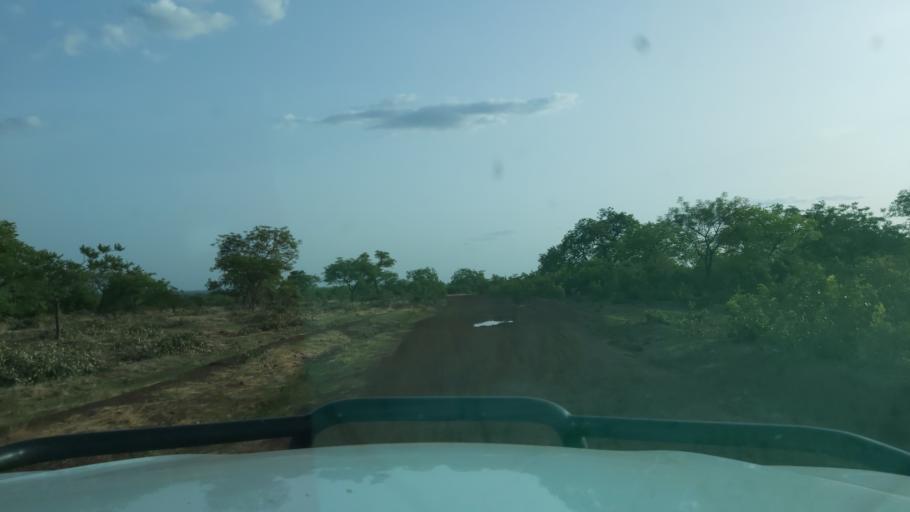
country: ML
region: Koulikoro
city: Kolokani
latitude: 13.2110
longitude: -7.9032
